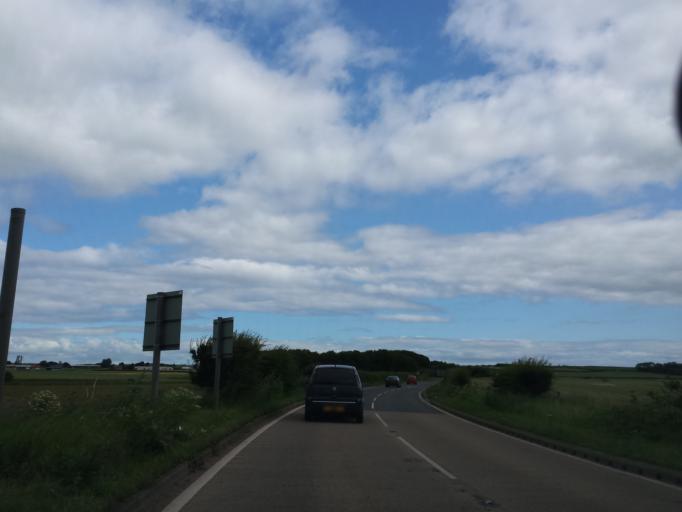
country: GB
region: Scotland
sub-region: East Lothian
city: Gullane
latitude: 56.0128
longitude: -2.7882
